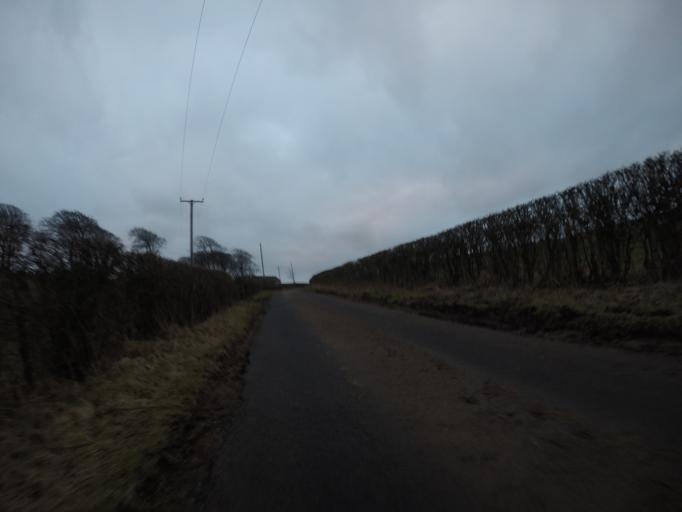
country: GB
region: Scotland
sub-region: North Ayrshire
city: Dalry
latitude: 55.6906
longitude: -4.7419
